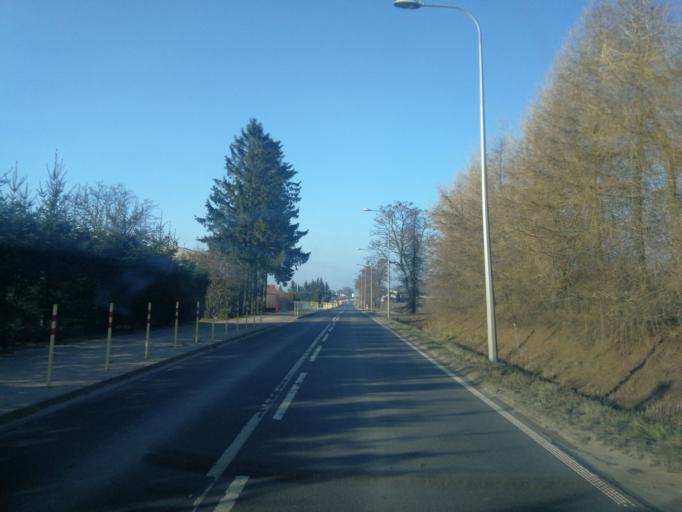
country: PL
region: Warmian-Masurian Voivodeship
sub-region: Powiat ilawski
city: Lubawa
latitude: 53.4821
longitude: 19.7627
